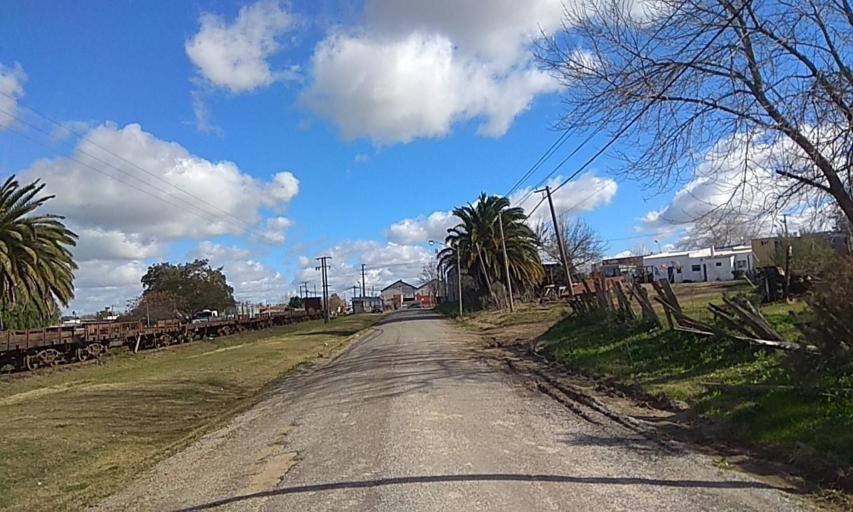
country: UY
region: Florida
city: Florida
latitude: -34.0868
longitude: -56.2127
